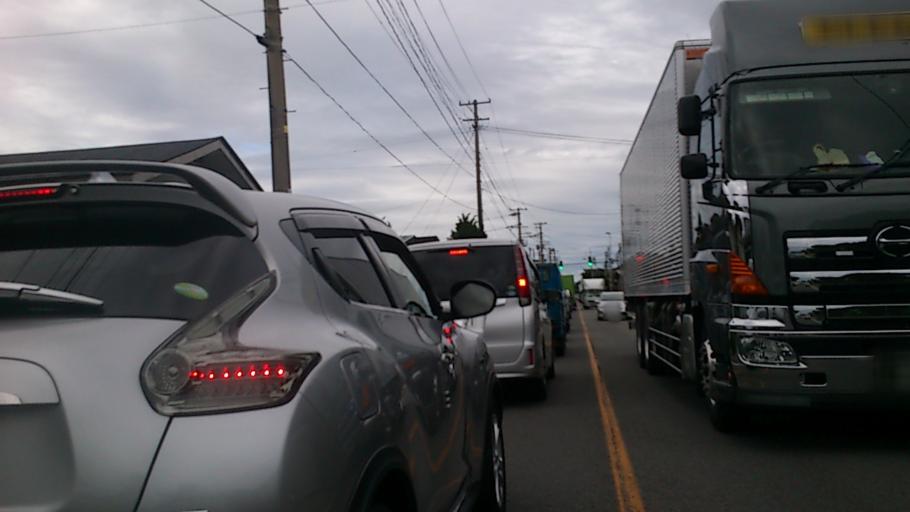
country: JP
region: Akita
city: Akita Shi
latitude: 39.6277
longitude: 140.0650
